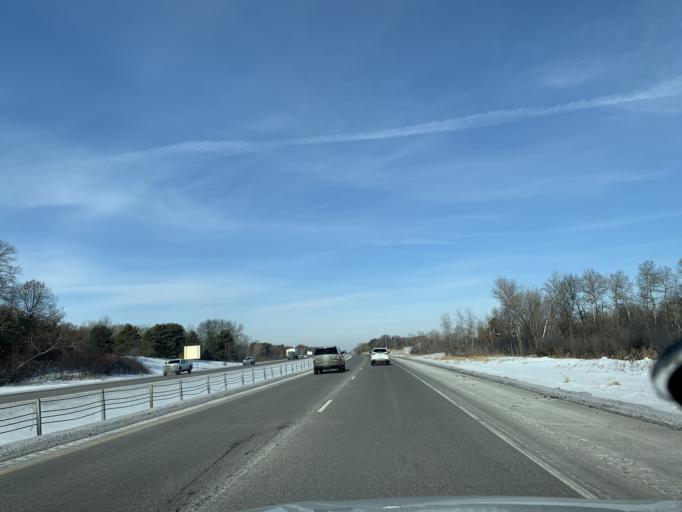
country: US
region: Minnesota
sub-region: Washington County
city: Forest Lake
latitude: 45.3007
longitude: -93.0025
